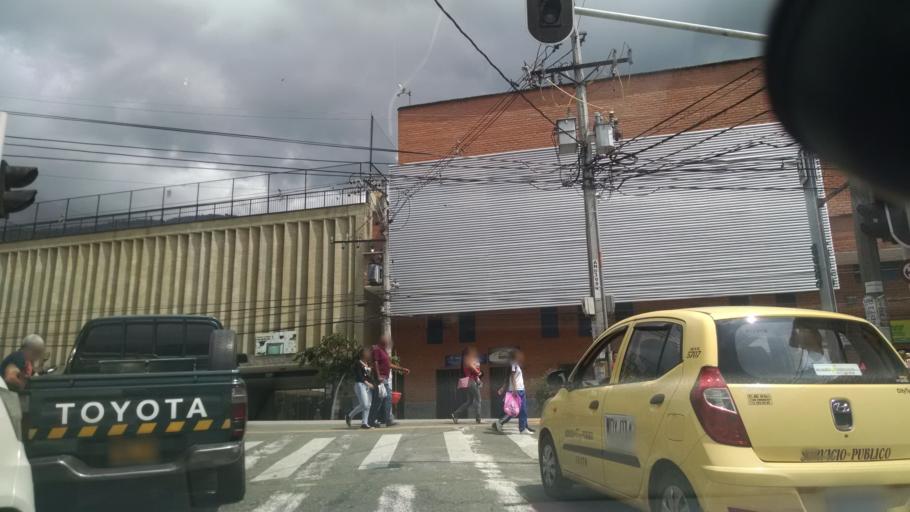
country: CO
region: Antioquia
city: Medellin
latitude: 6.2681
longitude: -75.5552
